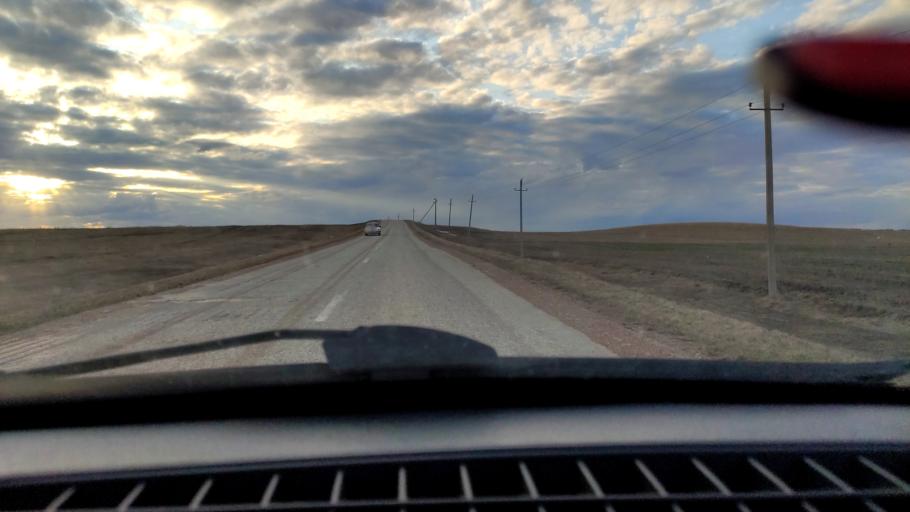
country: RU
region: Bashkortostan
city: Tolbazy
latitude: 54.0020
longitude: 55.6541
